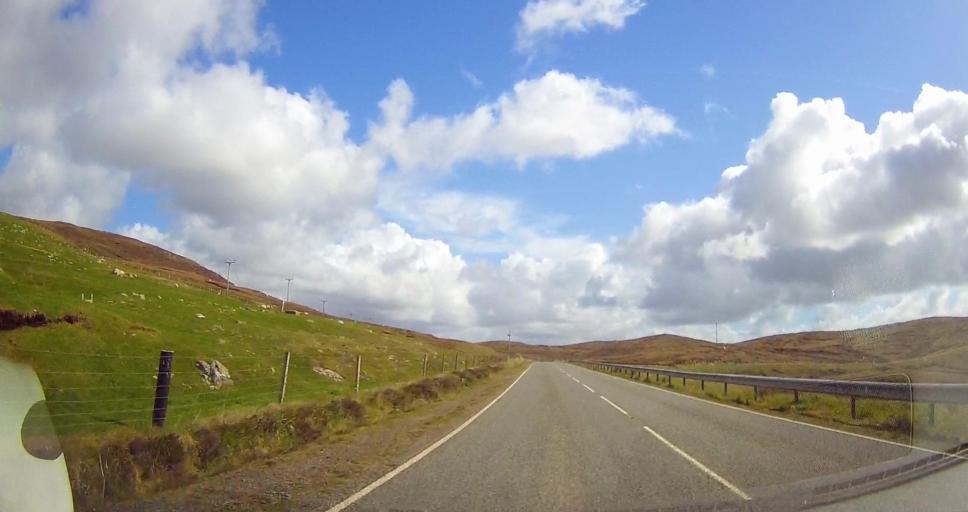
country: GB
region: Scotland
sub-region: Shetland Islands
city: Lerwick
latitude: 60.4629
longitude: -1.4048
